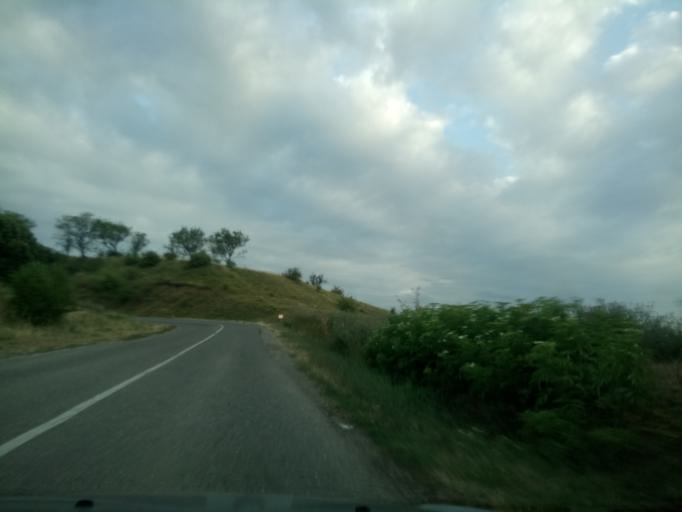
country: RS
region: Autonomna Pokrajina Vojvodina
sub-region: Sremski Okrug
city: Irig
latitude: 45.0933
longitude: 19.8660
